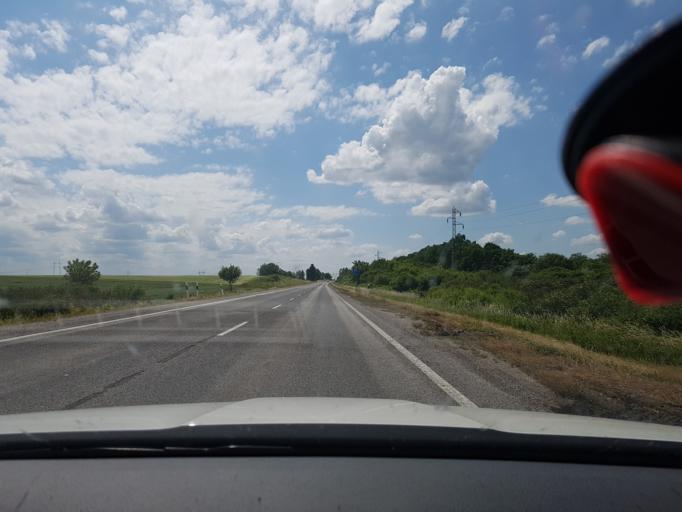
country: HU
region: Heves
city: Domoszlo
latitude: 47.7469
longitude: 20.1493
